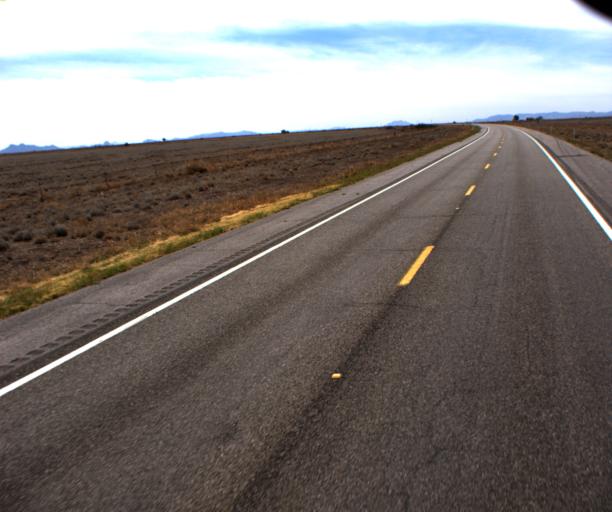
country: US
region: Arizona
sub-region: Cochise County
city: Pirtleville
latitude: 31.5665
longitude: -109.6678
